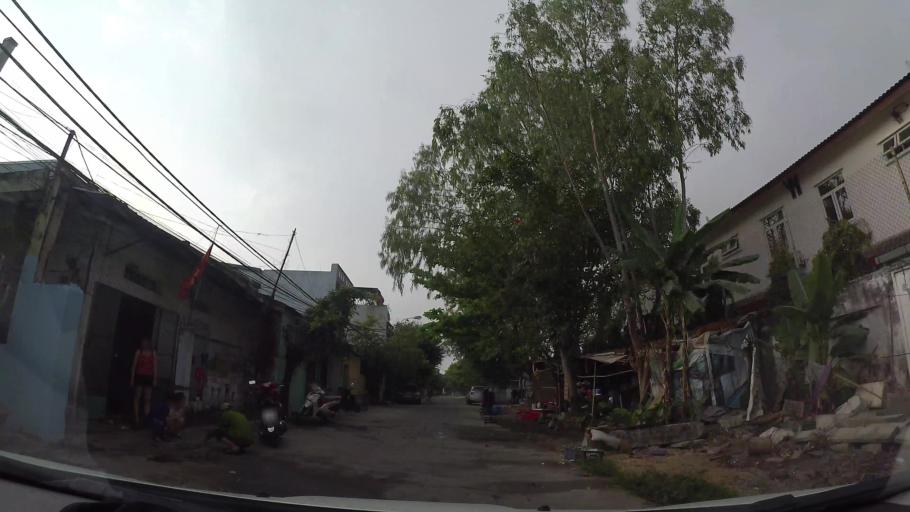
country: VN
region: Da Nang
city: Son Tra
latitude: 16.0814
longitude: 108.2397
